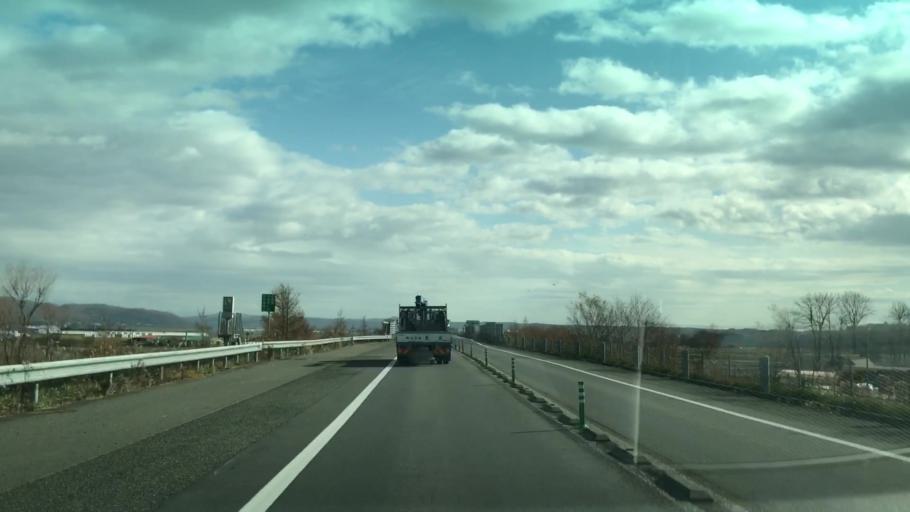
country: JP
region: Hokkaido
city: Tomakomai
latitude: 42.5791
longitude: 141.9555
